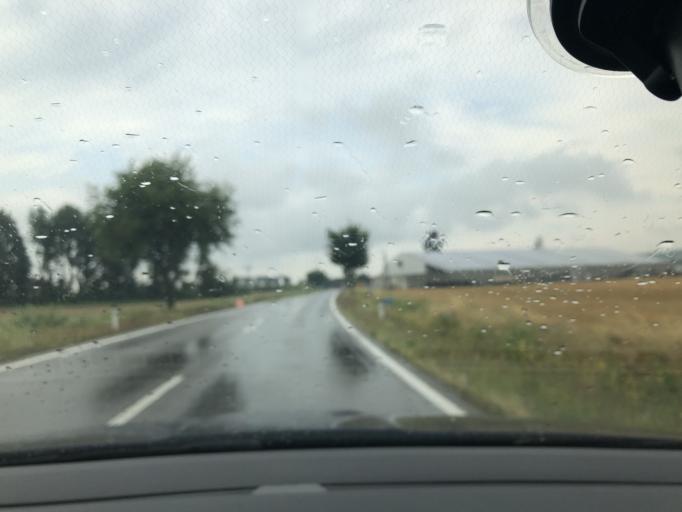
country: AT
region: Lower Austria
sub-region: Politischer Bezirk Ganserndorf
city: Gross-Schweinbarth
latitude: 48.3987
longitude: 16.6462
